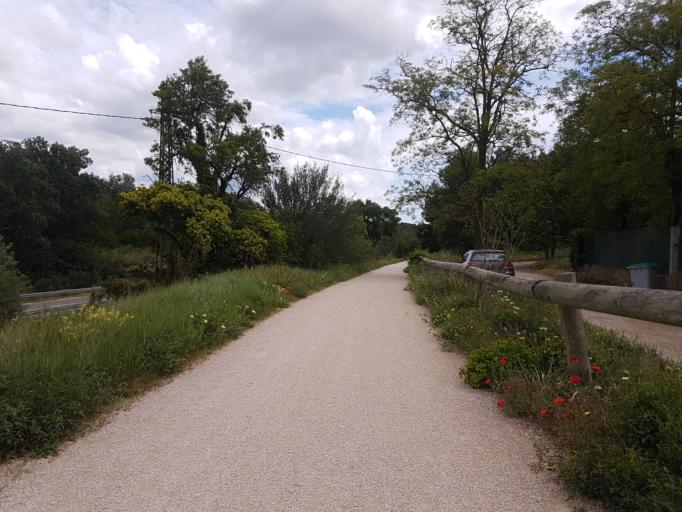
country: FR
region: Languedoc-Roussillon
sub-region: Departement du Gard
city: Vallabregues
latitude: 43.8294
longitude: 4.6197
